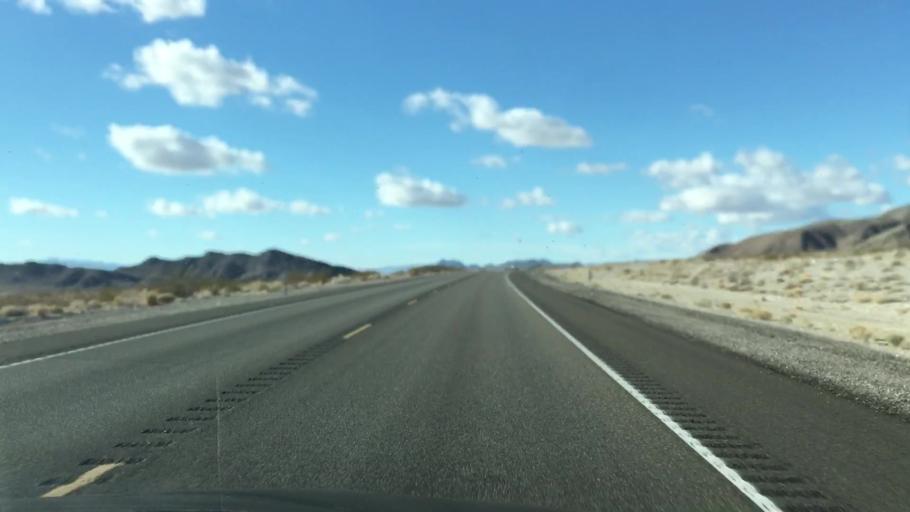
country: US
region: Nevada
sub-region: Nye County
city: Pahrump
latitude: 36.5737
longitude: -116.1846
